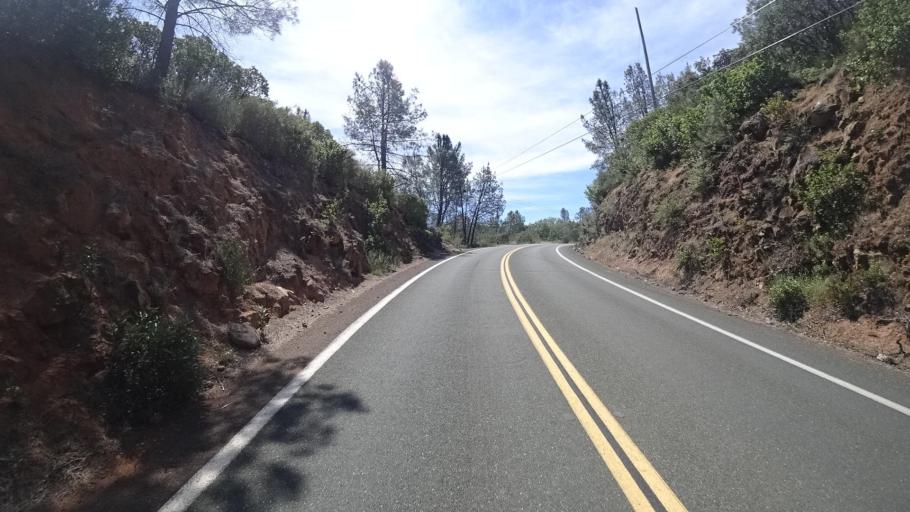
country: US
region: California
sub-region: Lake County
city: Clearlake
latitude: 38.9310
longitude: -122.6567
